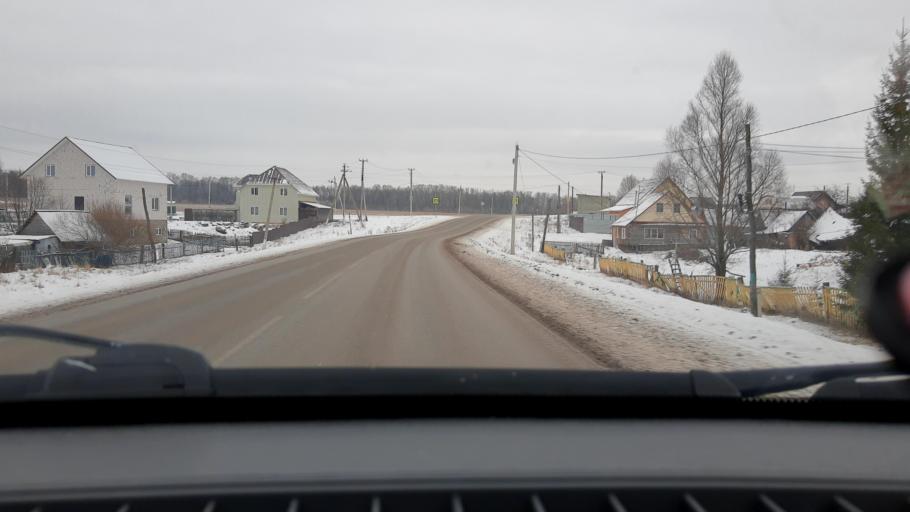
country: RU
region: Bashkortostan
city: Iglino
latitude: 54.8486
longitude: 56.4526
